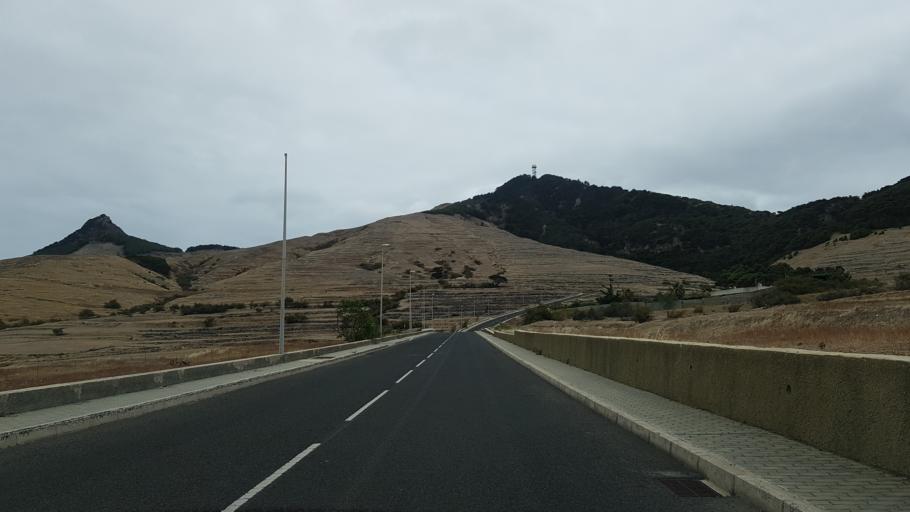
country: PT
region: Madeira
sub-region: Porto Santo
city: Camacha
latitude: 33.0892
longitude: -16.3387
